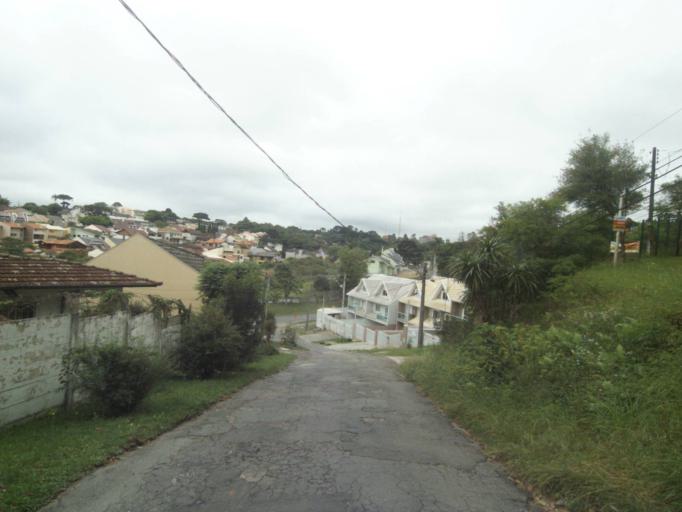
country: BR
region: Parana
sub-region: Curitiba
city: Curitiba
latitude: -25.3978
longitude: -49.2788
